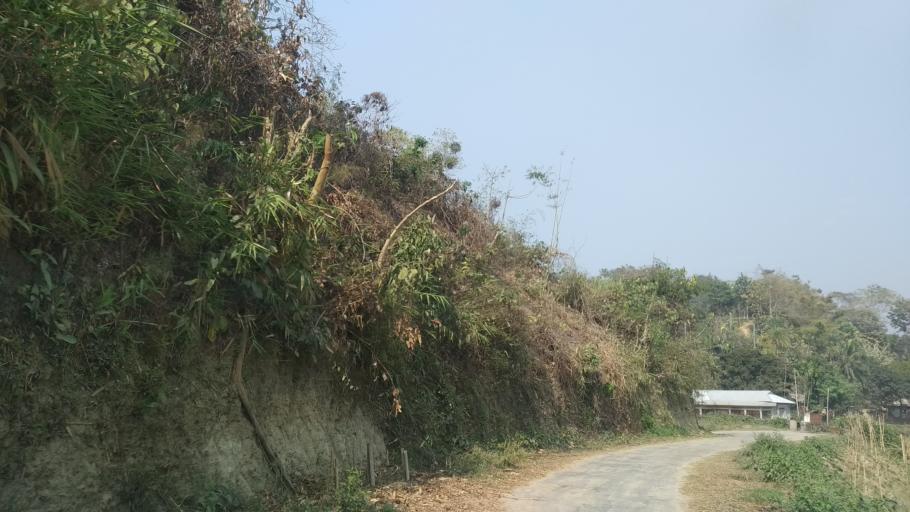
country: IN
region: Tripura
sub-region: West Tripura
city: Sonamura
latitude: 23.5235
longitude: 91.2590
